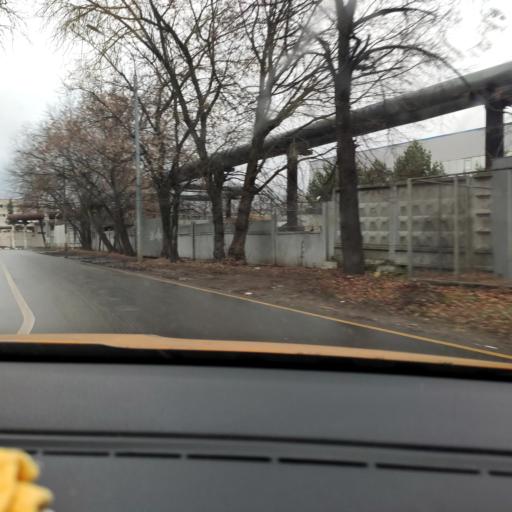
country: RU
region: Moscow
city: Lefortovo
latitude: 55.7423
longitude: 37.7194
